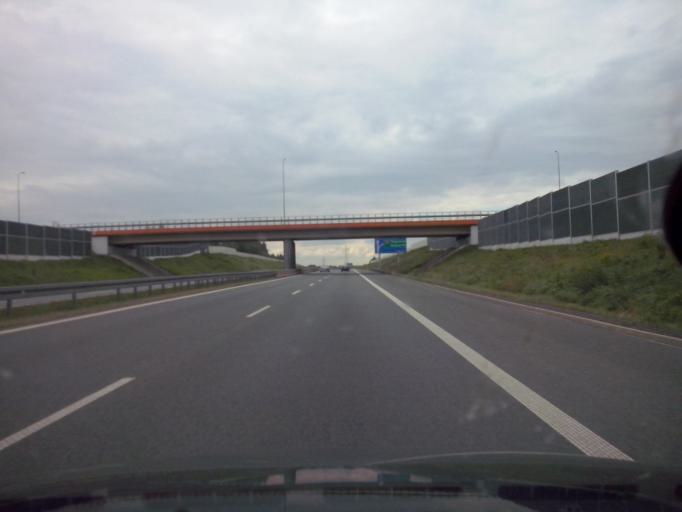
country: PL
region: Lesser Poland Voivodeship
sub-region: Powiat wielicki
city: Targowisko
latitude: 49.9871
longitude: 20.2964
